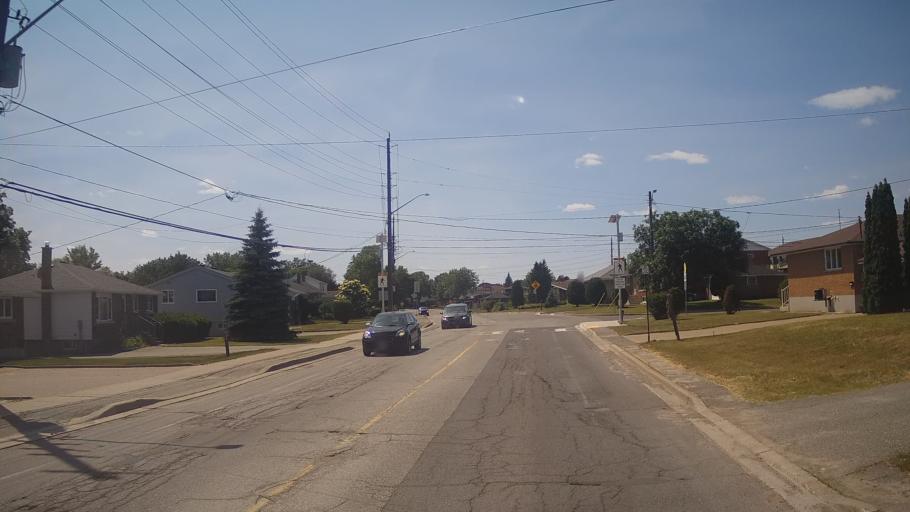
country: CA
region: Ontario
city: Greater Sudbury
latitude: 46.4599
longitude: -81.0255
